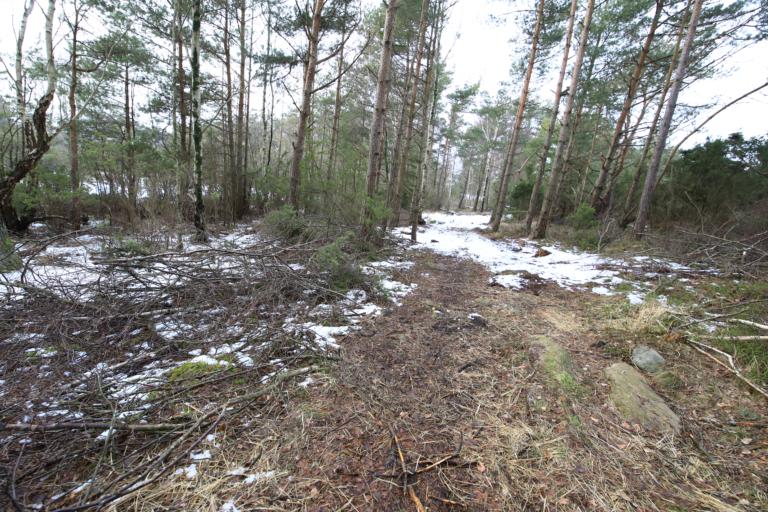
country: SE
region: Halland
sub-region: Kungsbacka Kommun
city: Frillesas
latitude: 57.2200
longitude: 12.1372
